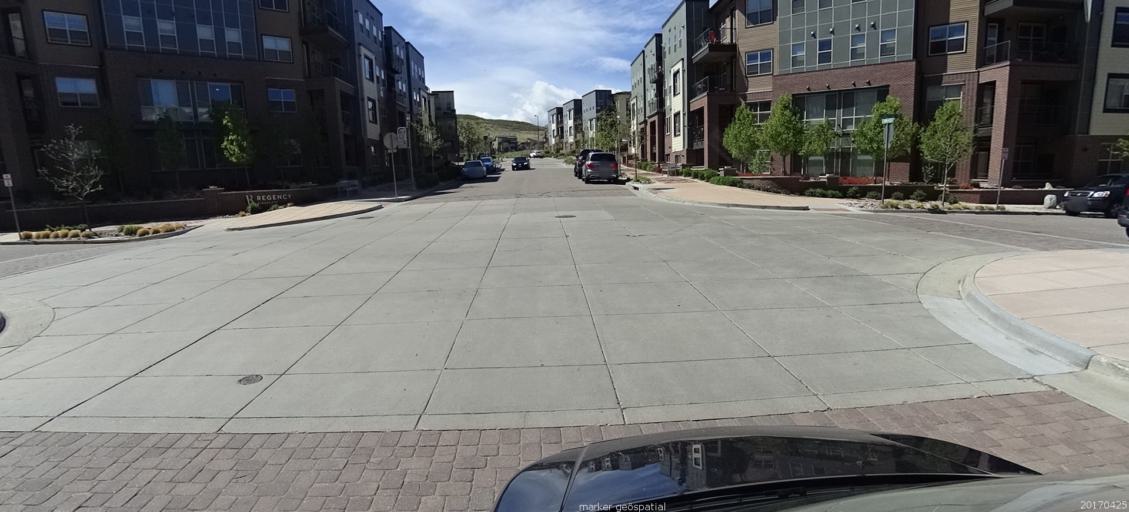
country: US
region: Colorado
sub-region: Douglas County
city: Carriage Club
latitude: 39.5294
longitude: -104.8780
